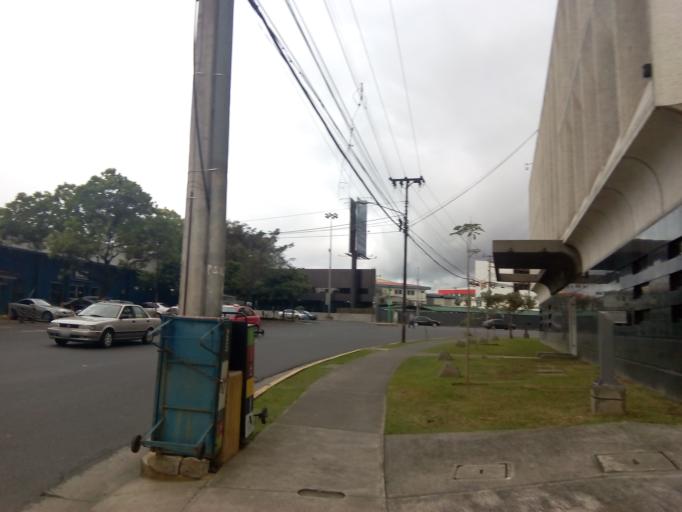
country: CR
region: San Jose
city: San Jose
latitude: 9.9424
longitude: -84.0776
